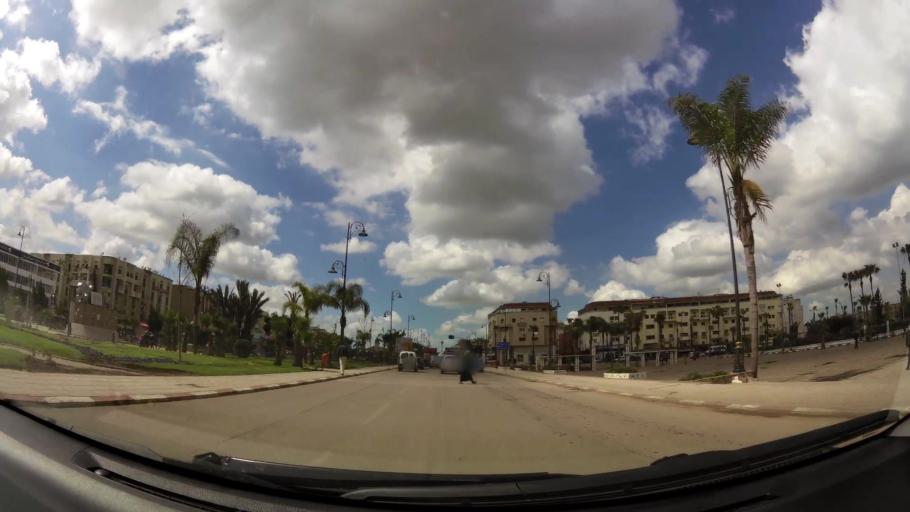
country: MA
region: Chaouia-Ouardigha
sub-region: Settat Province
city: Berrechid
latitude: 33.2660
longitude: -7.5828
